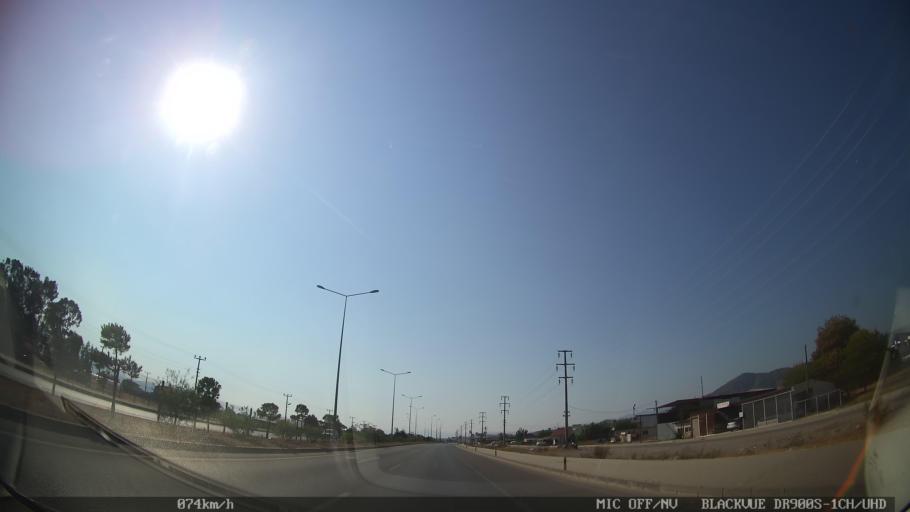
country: TR
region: Mugla
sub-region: Fethiye
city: Fethiye
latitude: 36.6542
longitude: 29.1675
